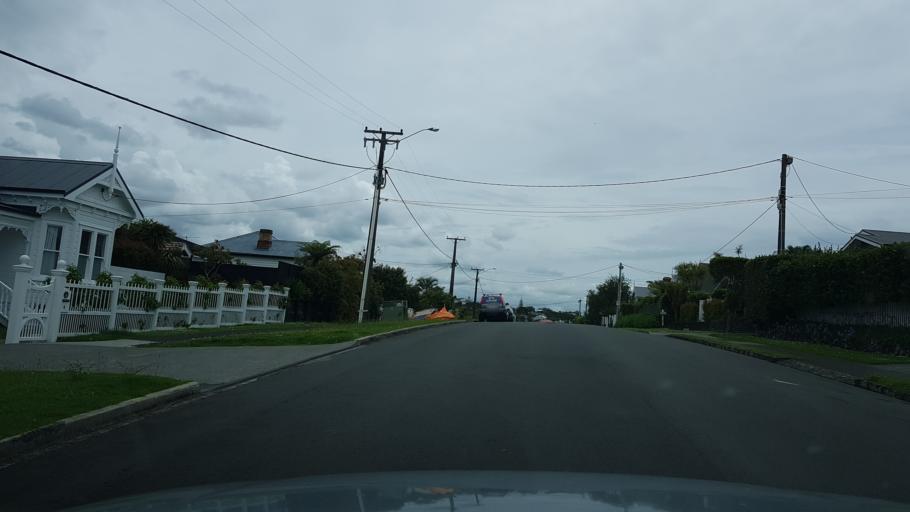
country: NZ
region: Auckland
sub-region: Auckland
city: North Shore
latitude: -36.8206
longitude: 174.7330
